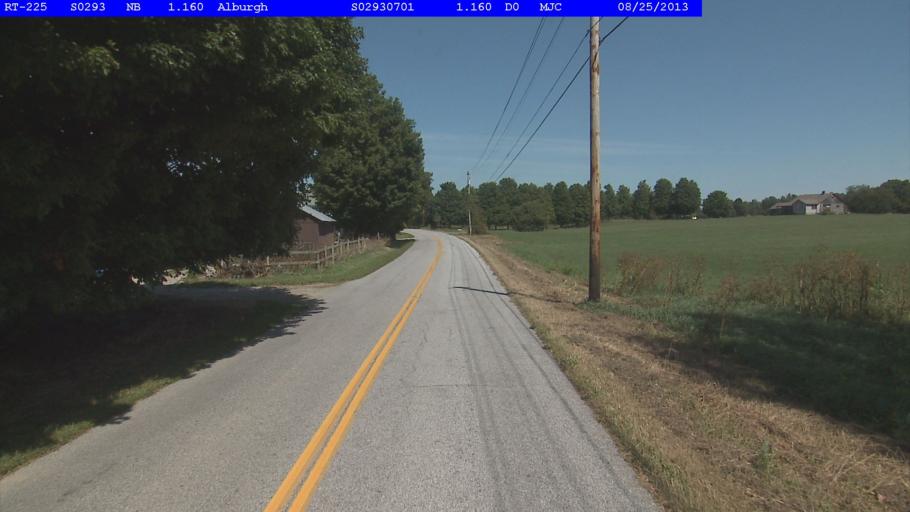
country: US
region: New York
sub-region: Clinton County
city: Rouses Point
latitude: 45.0053
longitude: -73.2954
